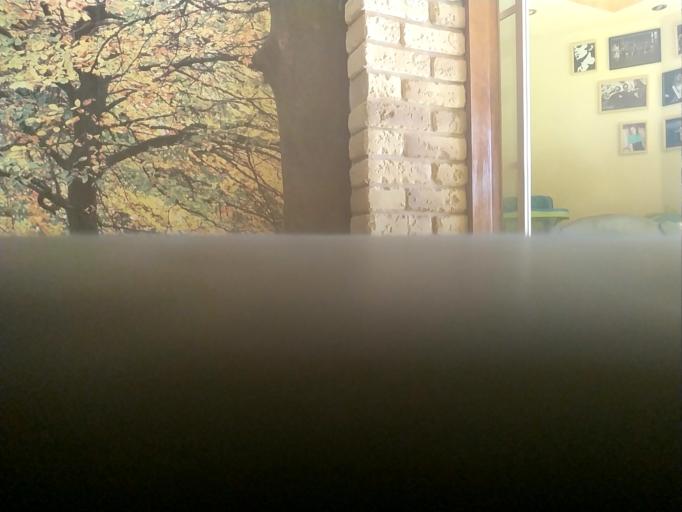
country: RU
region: Smolensk
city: Temkino
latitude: 55.1009
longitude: 34.8994
